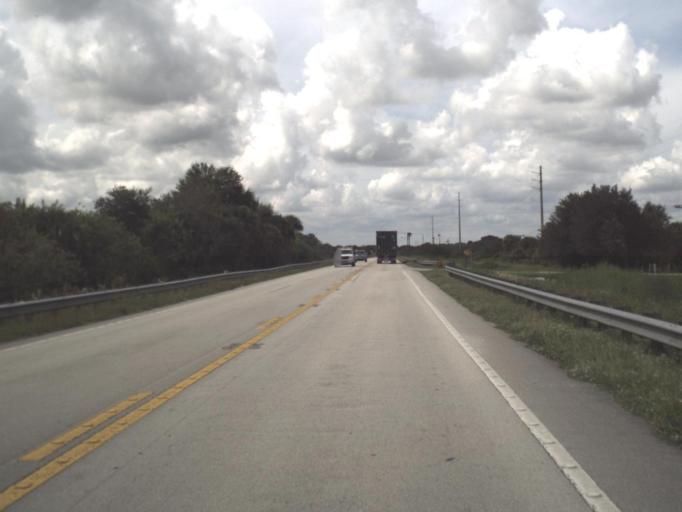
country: US
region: Florida
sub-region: Glades County
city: Buckhead Ridge
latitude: 27.2424
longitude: -80.9745
